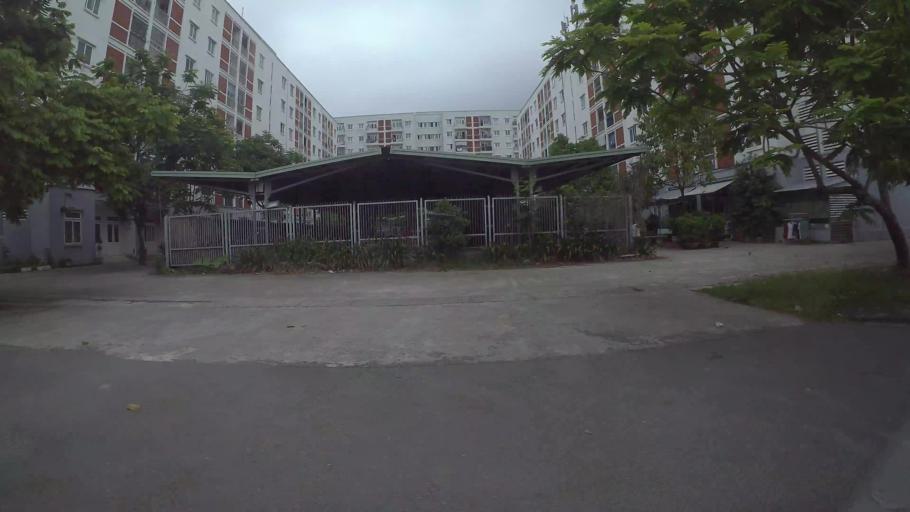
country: VN
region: Da Nang
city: Thanh Khe
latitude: 16.0440
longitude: 108.1757
